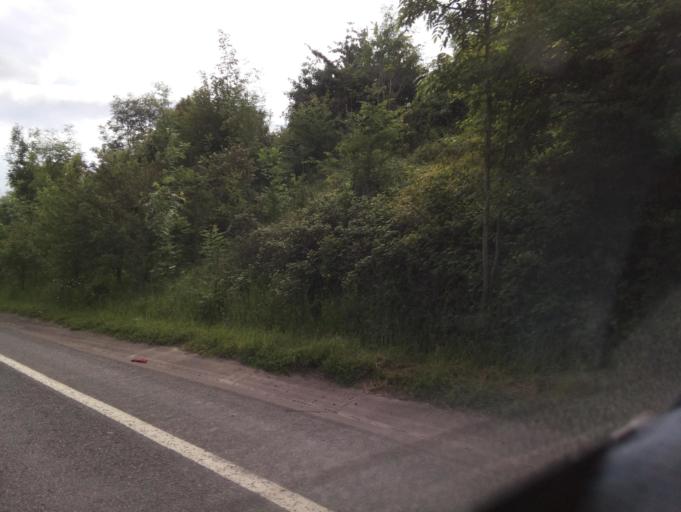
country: GB
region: England
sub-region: Worcestershire
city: Bransford
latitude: 52.1836
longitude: -2.2745
